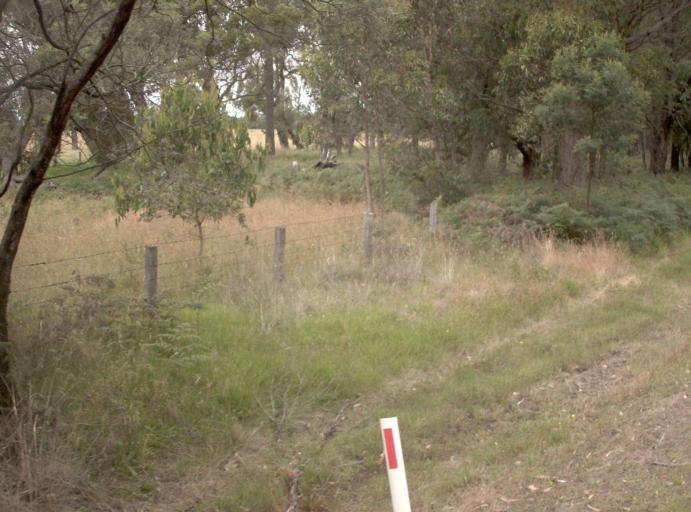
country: AU
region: Victoria
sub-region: Latrobe
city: Traralgon
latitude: -38.5008
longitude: 146.8343
